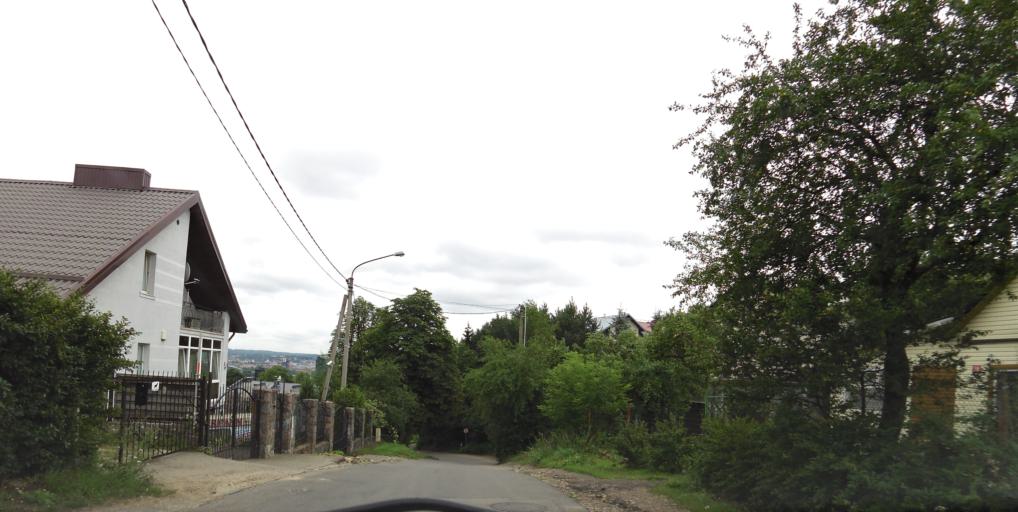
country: LT
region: Vilnius County
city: Seskine
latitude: 54.7056
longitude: 25.2542
